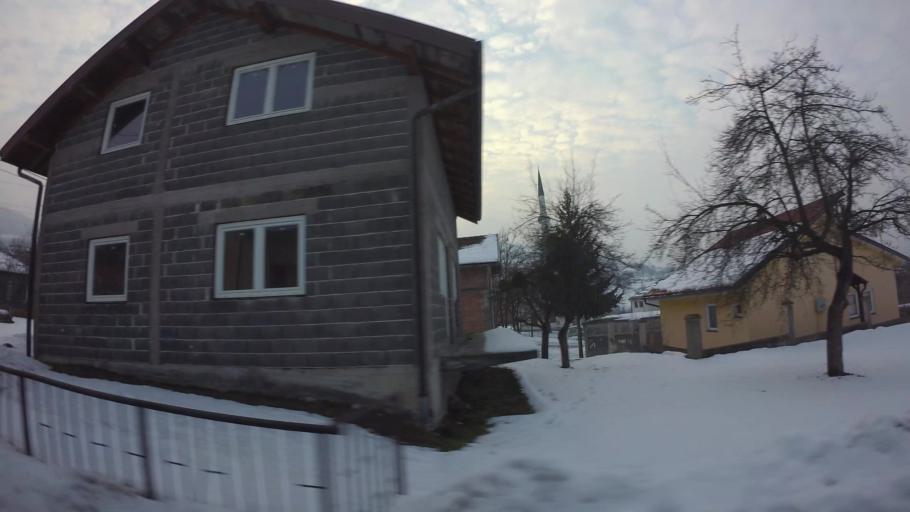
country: BA
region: Federation of Bosnia and Herzegovina
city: Hotonj
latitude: 43.8922
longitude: 18.3635
